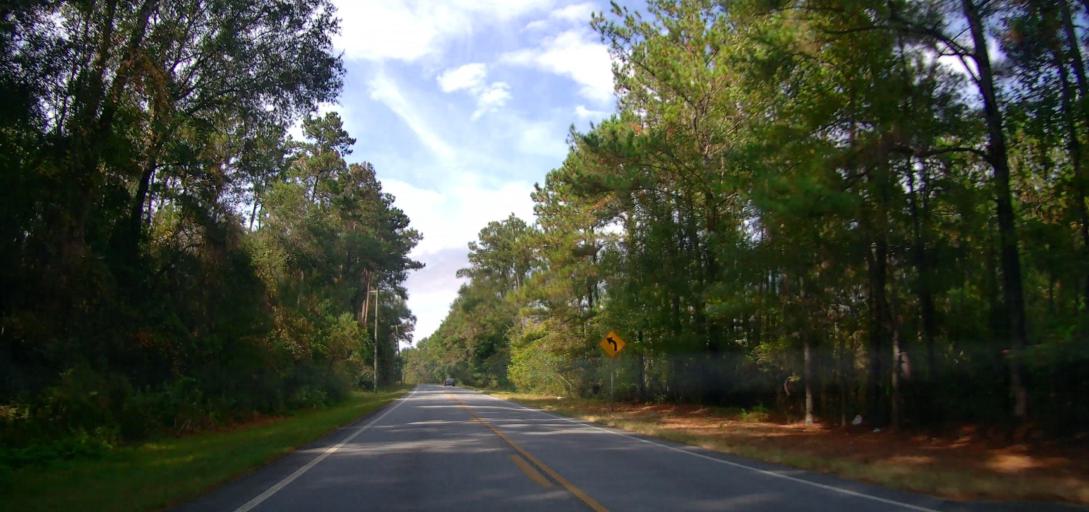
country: US
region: Georgia
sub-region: Thomas County
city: Thomasville
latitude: 30.9196
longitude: -84.0124
